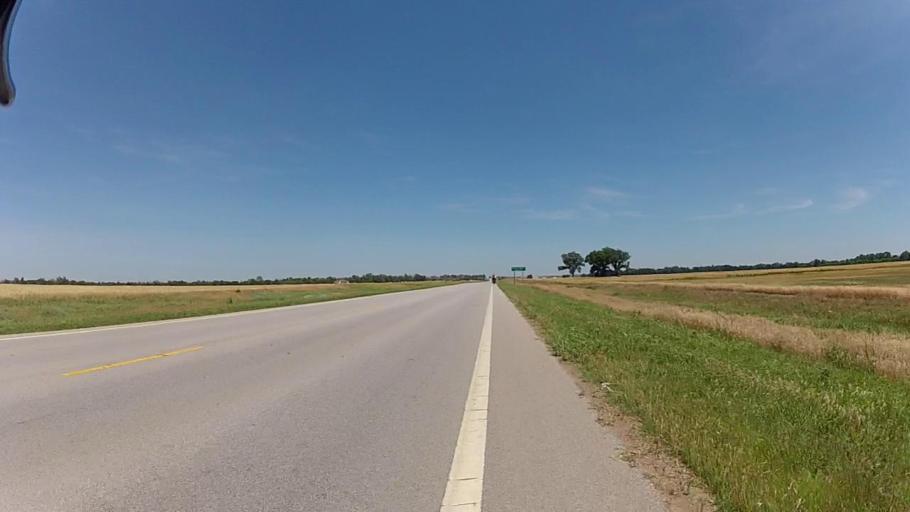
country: US
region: Kansas
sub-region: Harper County
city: Harper
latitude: 37.2387
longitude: -98.1322
